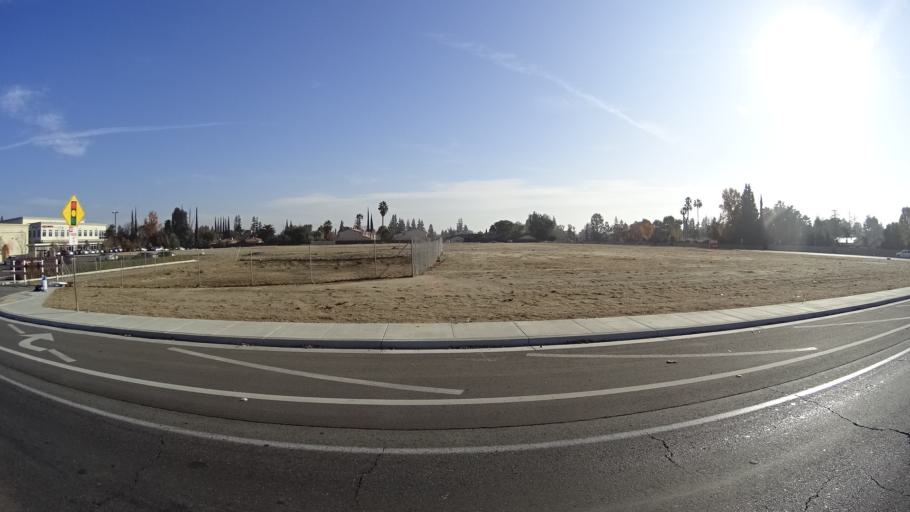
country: US
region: California
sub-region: Kern County
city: Greenacres
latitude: 35.3547
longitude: -119.0921
